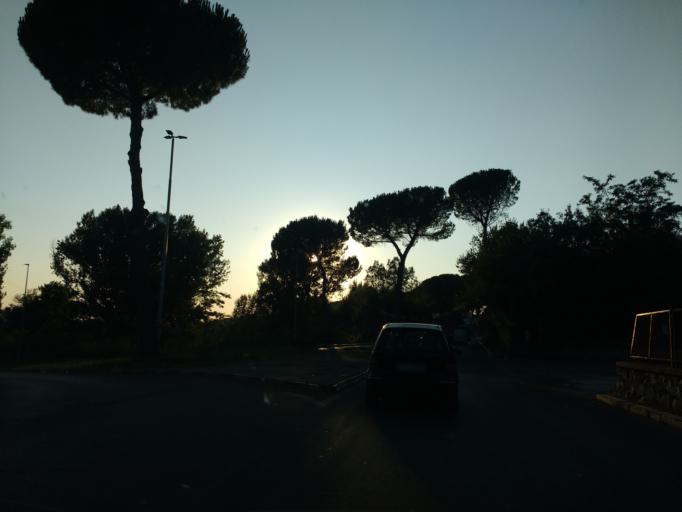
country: IT
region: Latium
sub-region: Citta metropolitana di Roma Capitale
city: Villa Adriana
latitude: 41.9553
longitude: 12.7640
